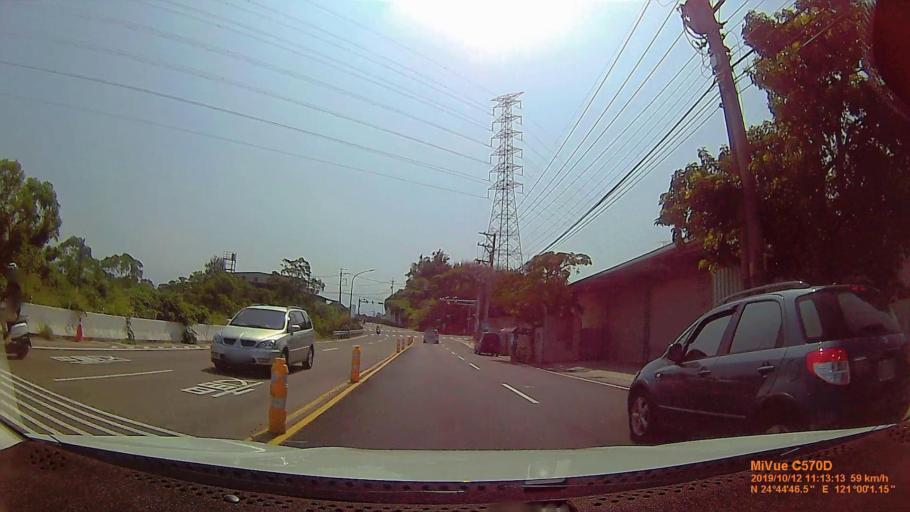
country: TW
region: Taiwan
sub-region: Hsinchu
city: Hsinchu
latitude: 24.7461
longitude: 121.0004
